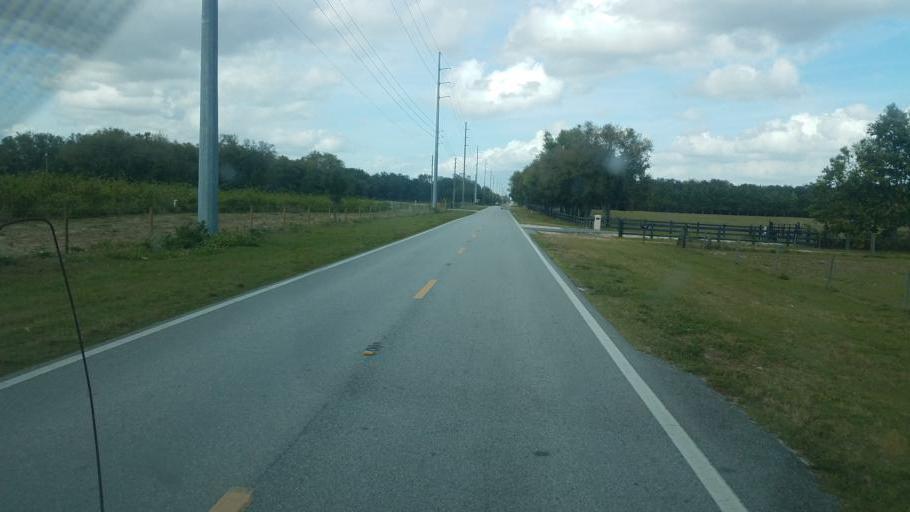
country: US
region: Florida
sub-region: Polk County
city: Lake Wales
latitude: 27.9373
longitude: -81.5377
